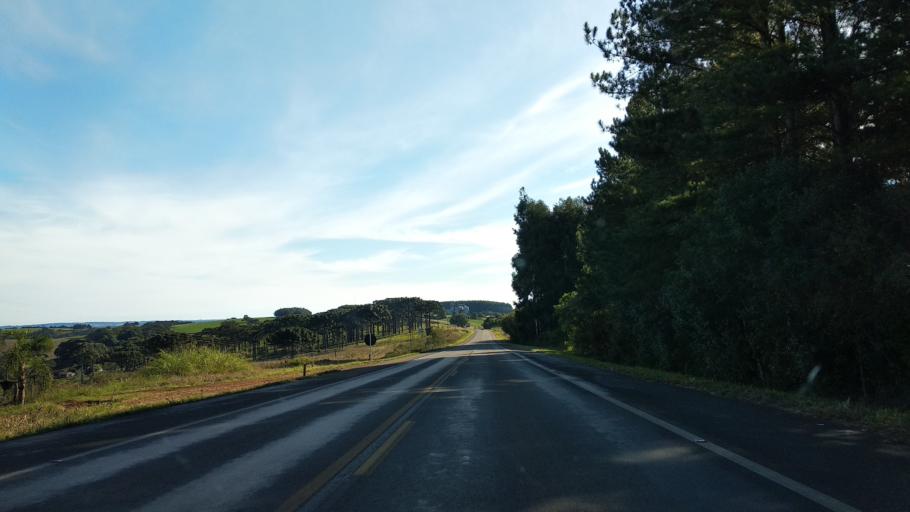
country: BR
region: Santa Catarina
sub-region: Celso Ramos
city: Celso Ramos
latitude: -27.5270
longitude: -51.3678
